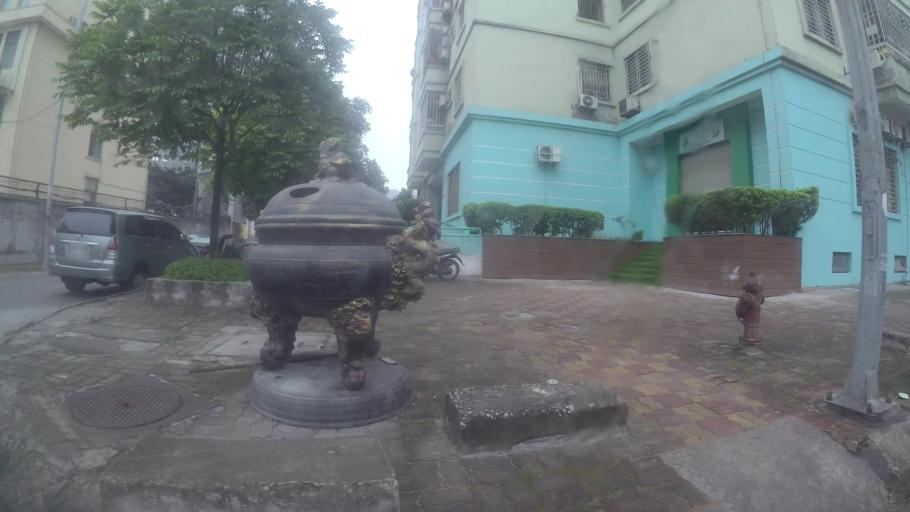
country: VN
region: Ha Noi
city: Cau Giay
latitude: 21.0225
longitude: 105.7880
